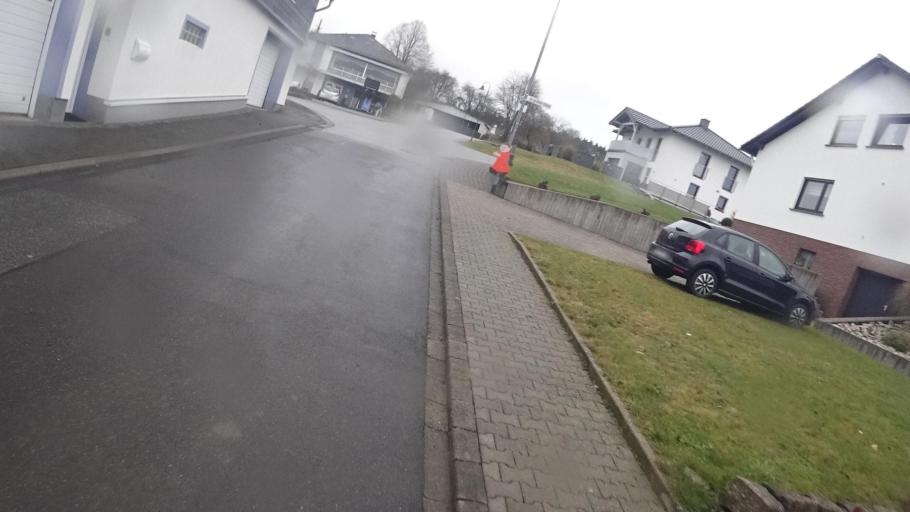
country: DE
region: Rheinland-Pfalz
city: Maisborn
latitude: 50.0787
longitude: 7.6054
